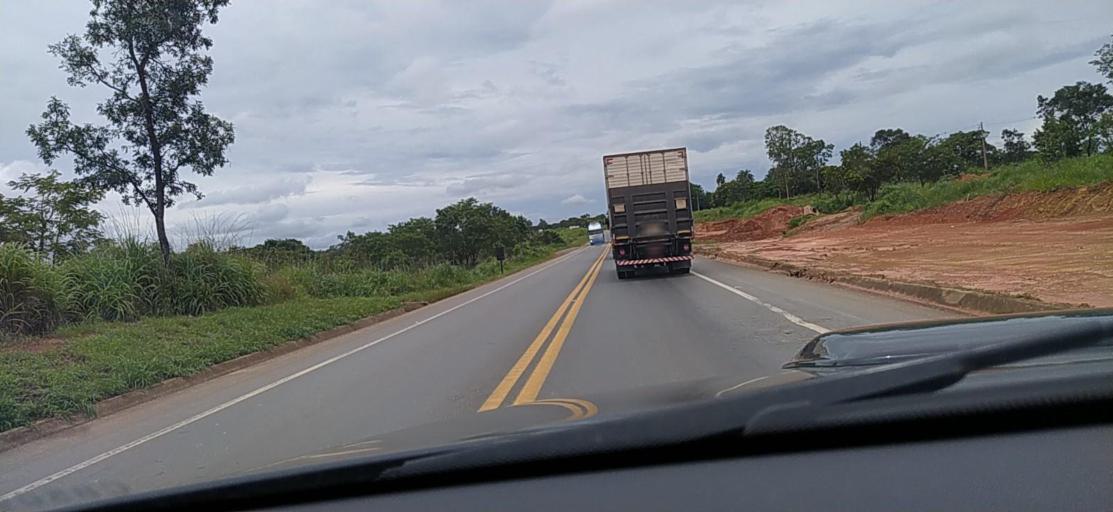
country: BR
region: Minas Gerais
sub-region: Curvelo
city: Curvelo
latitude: -18.7271
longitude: -44.4422
